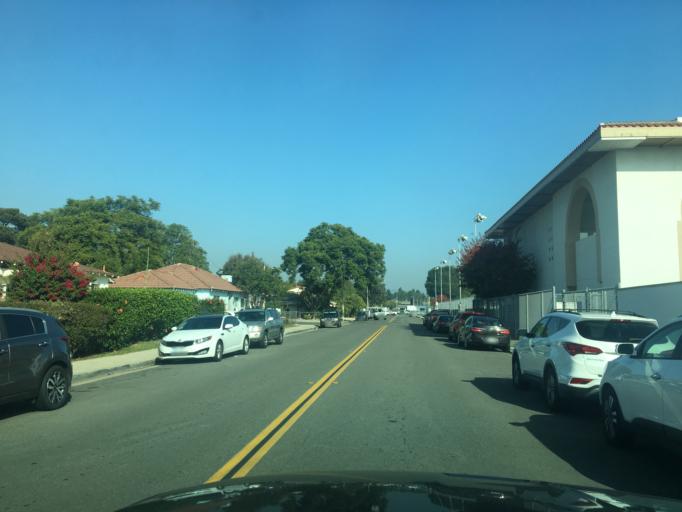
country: US
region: California
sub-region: Orange County
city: Tustin
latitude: 33.7384
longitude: -117.8191
